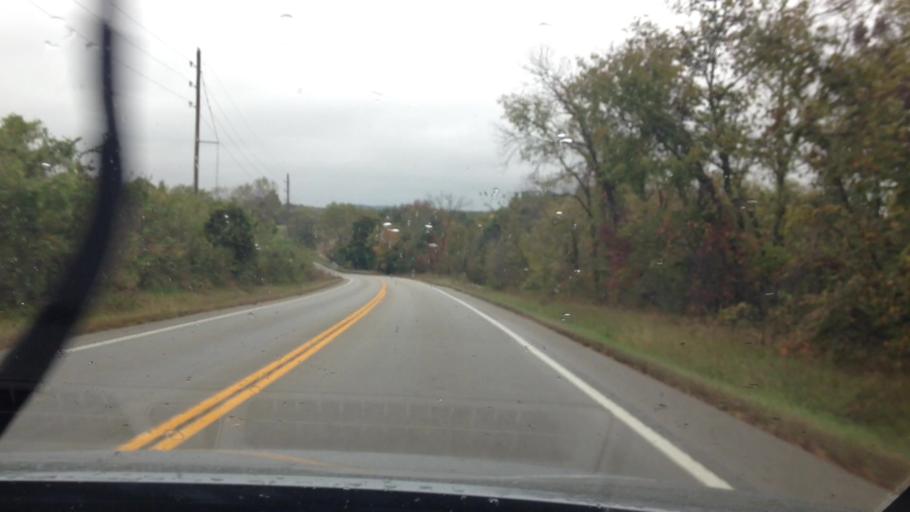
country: US
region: Missouri
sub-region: Platte County
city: Weston
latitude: 39.4083
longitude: -94.8692
